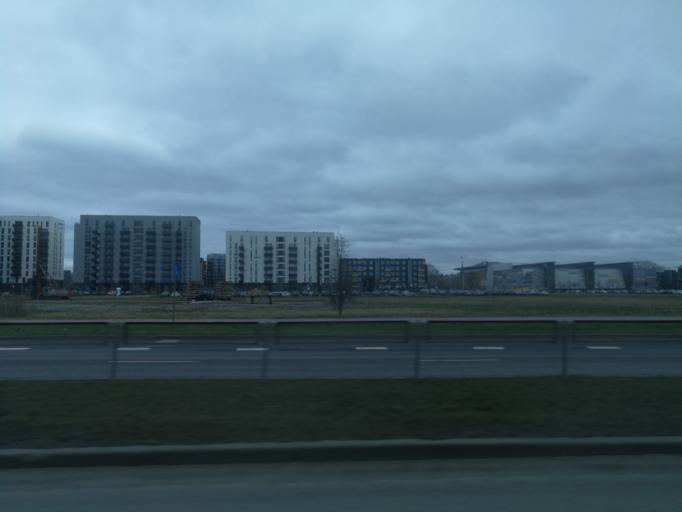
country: LV
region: Riga
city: Riga
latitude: 56.9709
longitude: 24.1202
